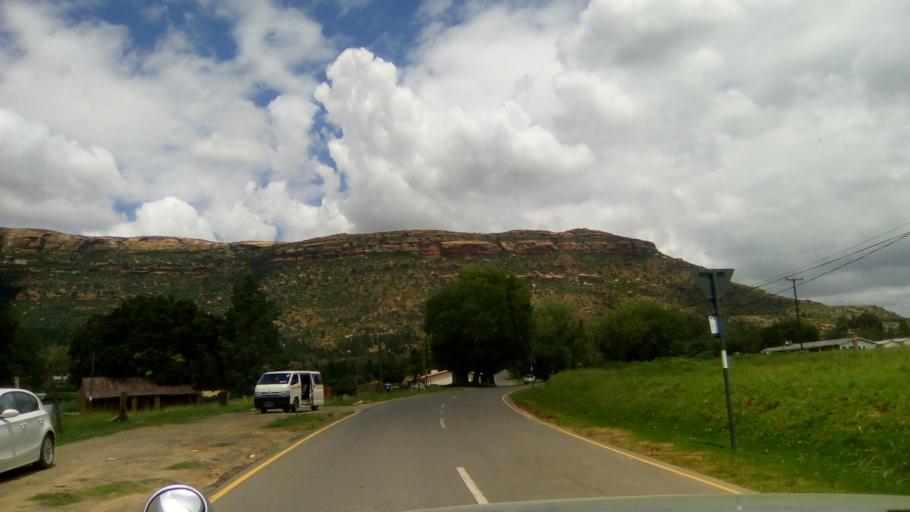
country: LS
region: Maseru
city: Nako
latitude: -29.6259
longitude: 27.5033
